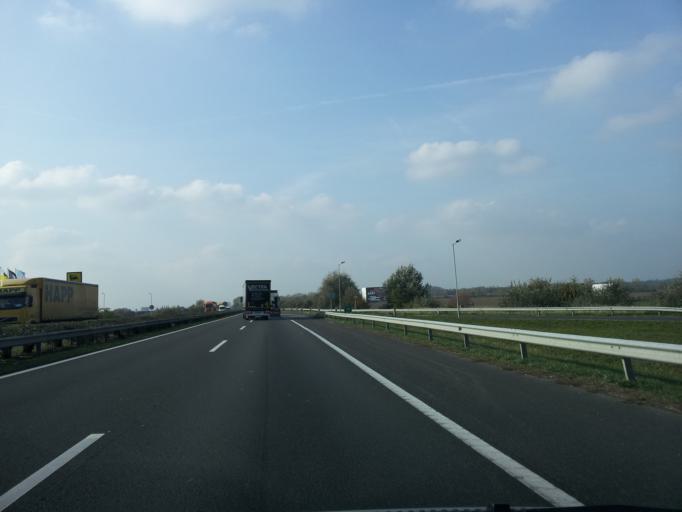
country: HU
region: Pest
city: Zsambek
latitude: 47.5110
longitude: 18.7360
